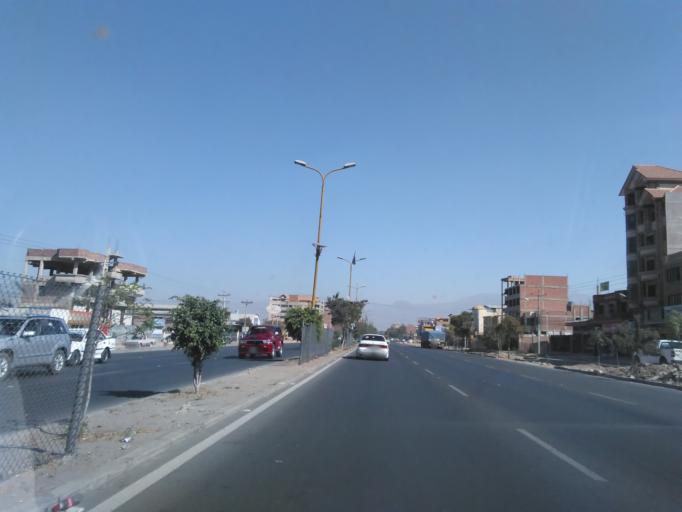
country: BO
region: Cochabamba
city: Cochabamba
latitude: -17.3910
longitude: -66.2351
